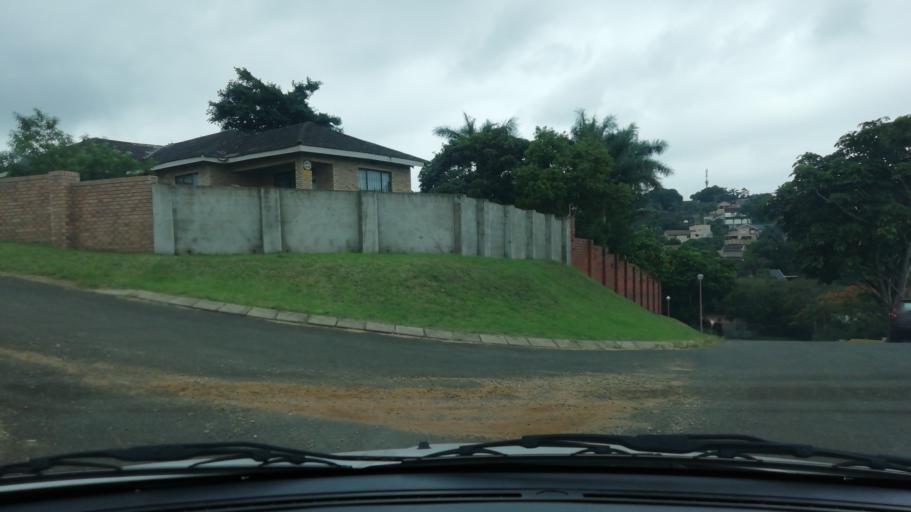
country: ZA
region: KwaZulu-Natal
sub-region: uThungulu District Municipality
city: Empangeni
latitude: -28.7586
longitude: 31.8846
